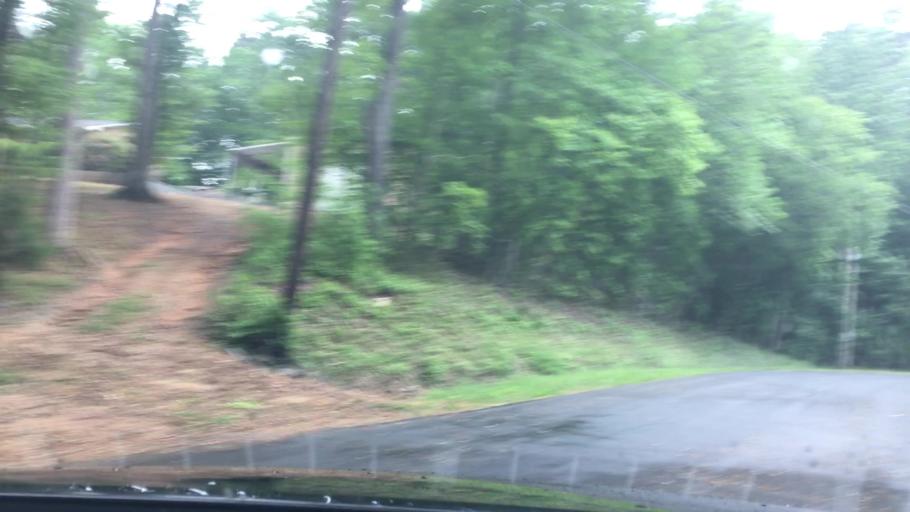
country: US
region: North Carolina
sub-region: Stanly County
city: Badin
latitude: 35.3582
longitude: -80.1168
